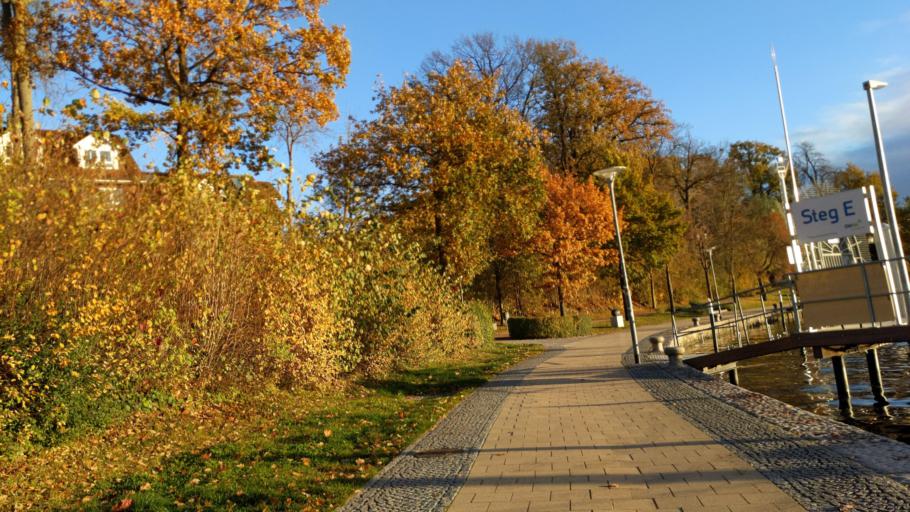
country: DE
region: Schleswig-Holstein
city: Neustadt in Holstein
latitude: 54.0997
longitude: 10.8139
